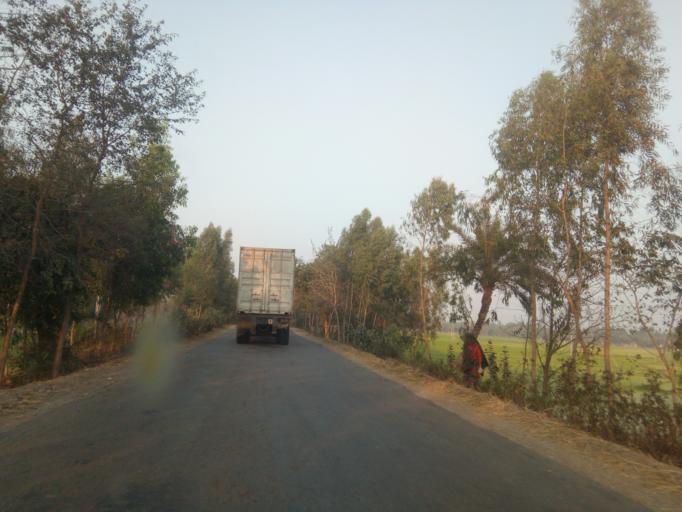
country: BD
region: Rajshahi
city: Bogra
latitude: 24.5501
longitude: 89.1913
